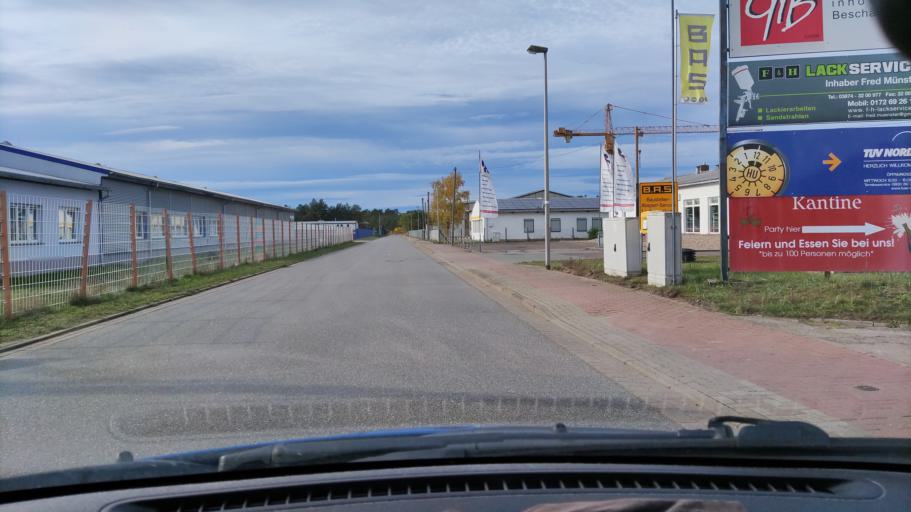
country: DE
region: Mecklenburg-Vorpommern
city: Ludwigslust
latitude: 53.3103
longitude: 11.5095
